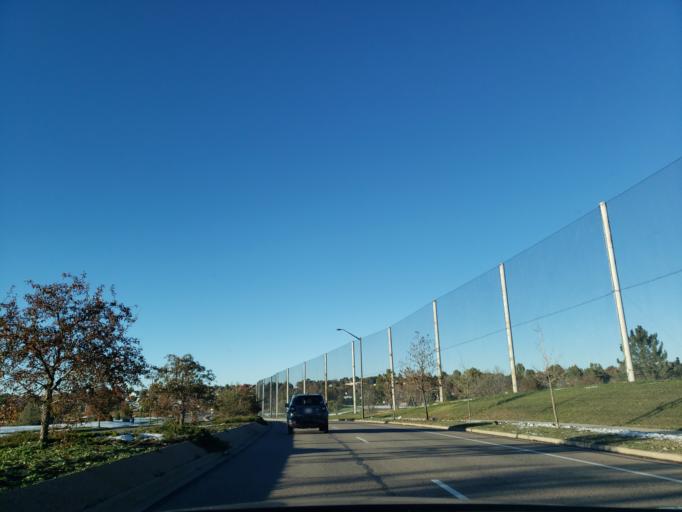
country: US
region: Colorado
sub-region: Larimer County
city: Fort Collins
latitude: 40.5036
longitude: -105.0576
